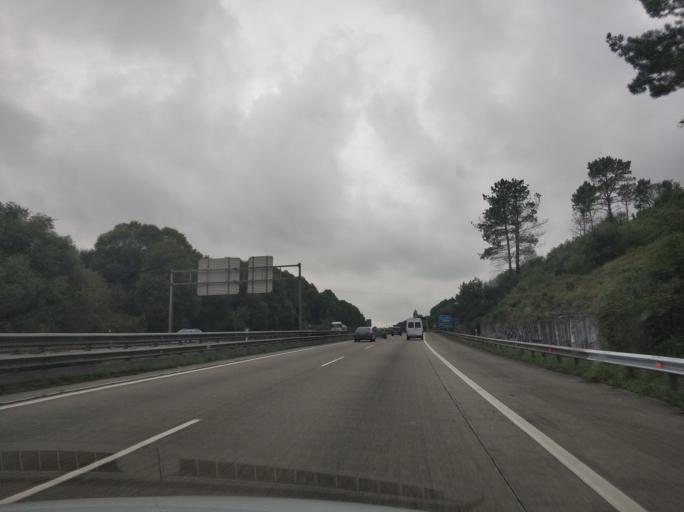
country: ES
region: Asturias
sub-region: Province of Asturias
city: Corvera de Asturias
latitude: 43.5058
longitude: -5.8054
